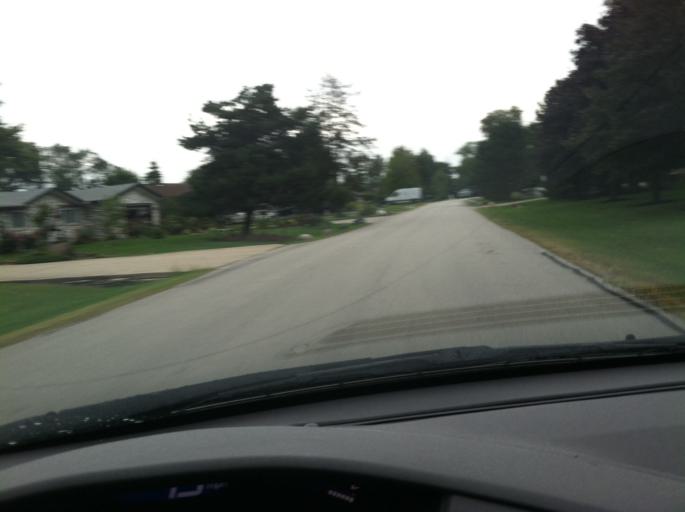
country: US
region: Illinois
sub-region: DuPage County
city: Wood Dale
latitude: 41.9732
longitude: -87.9632
